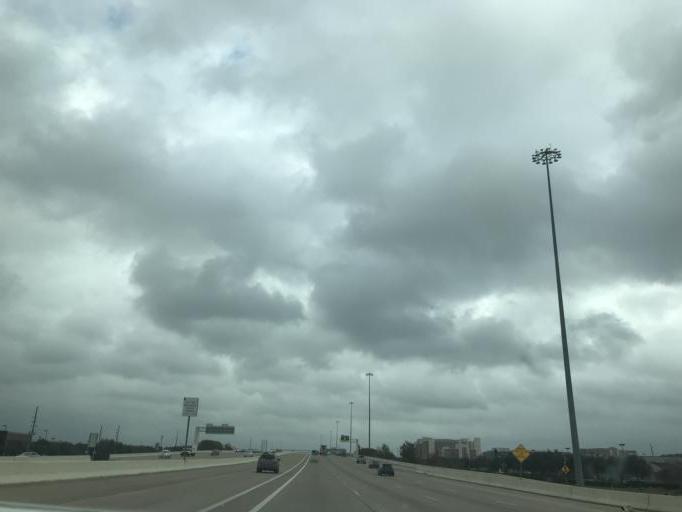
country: US
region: Texas
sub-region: Fort Bend County
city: Sugar Land
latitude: 29.5872
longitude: -95.6378
